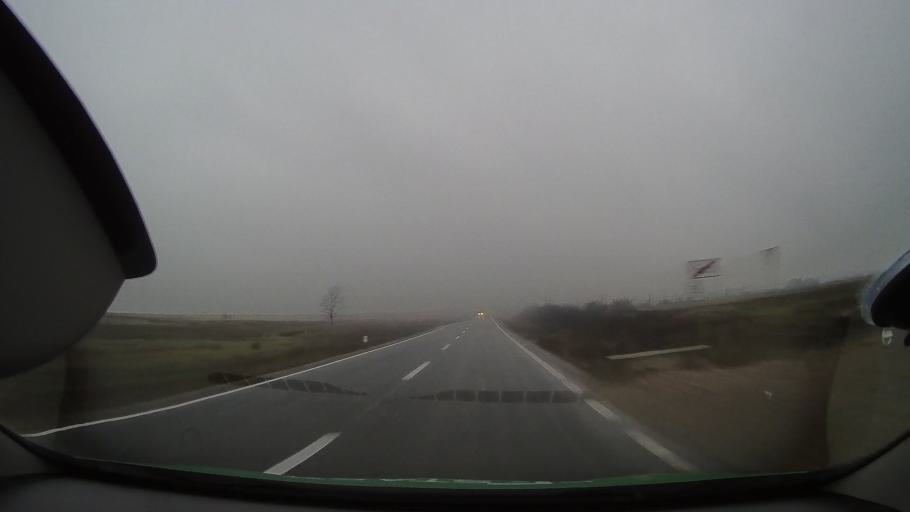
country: RO
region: Arad
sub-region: Comuna Craiova
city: Craiova
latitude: 46.6274
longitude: 21.9586
